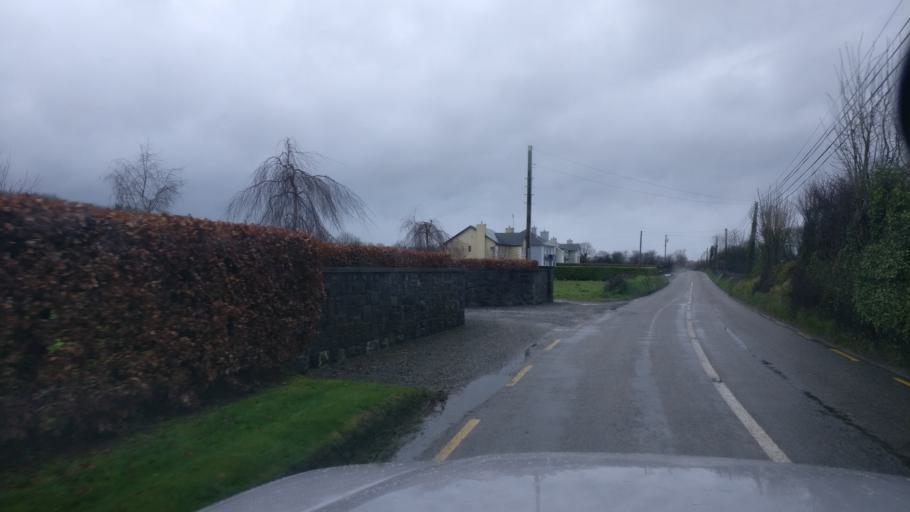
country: IE
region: Connaught
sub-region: County Galway
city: Portumna
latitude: 53.0944
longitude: -8.2664
